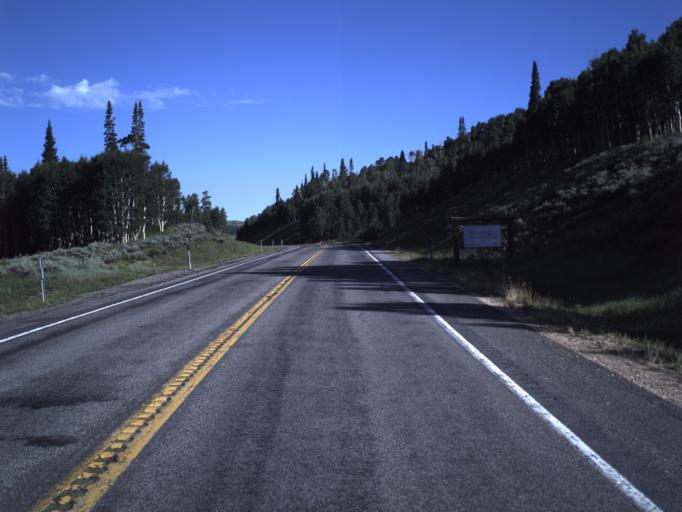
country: US
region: Utah
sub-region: Sanpete County
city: Fairview
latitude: 39.5845
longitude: -111.2582
